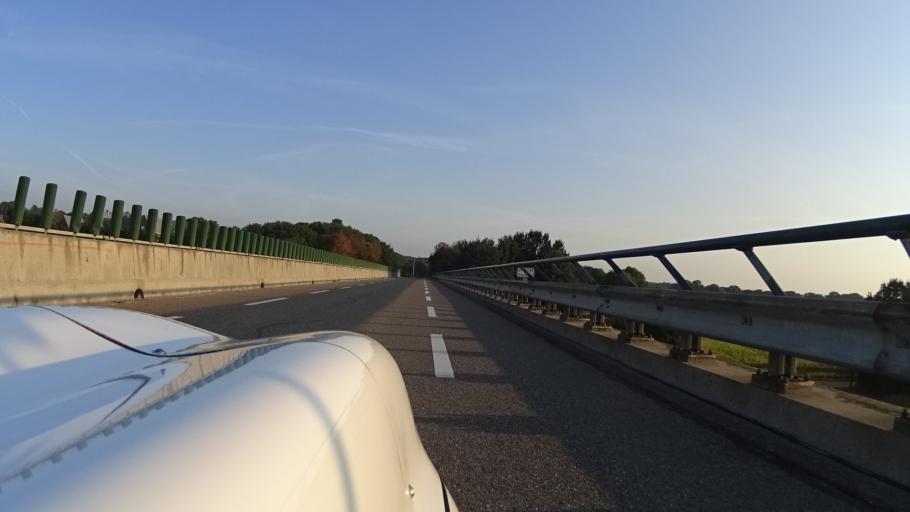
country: NL
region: Limburg
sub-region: Gemeente Bergen
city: Wellerlooi
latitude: 51.5488
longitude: 6.0992
